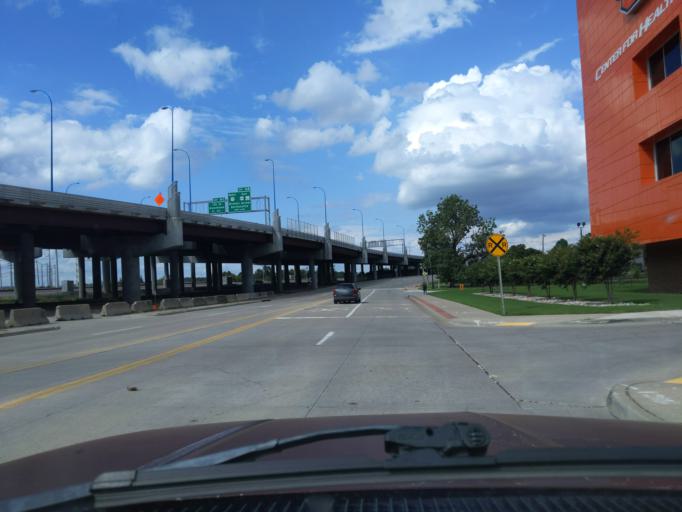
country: US
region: Oklahoma
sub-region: Tulsa County
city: Tulsa
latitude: 36.1387
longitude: -96.0069
